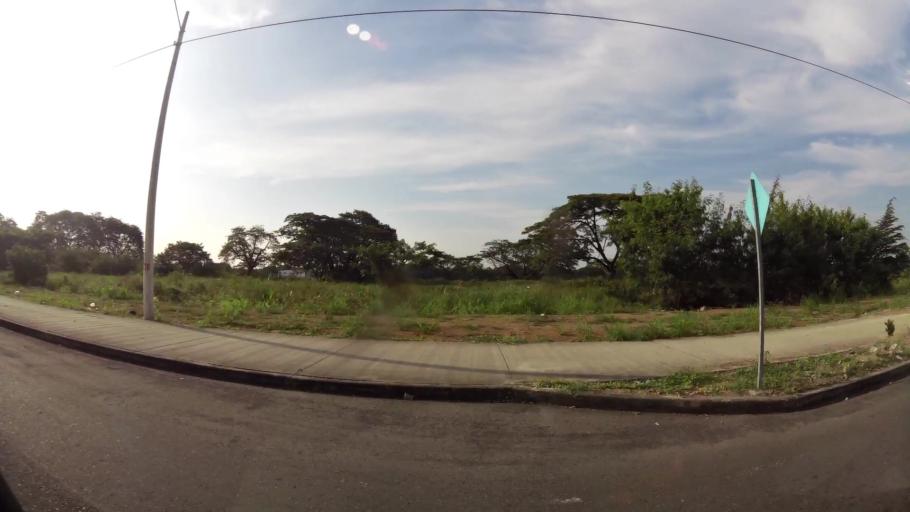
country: EC
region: Guayas
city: Eloy Alfaro
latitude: -2.0601
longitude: -79.8859
